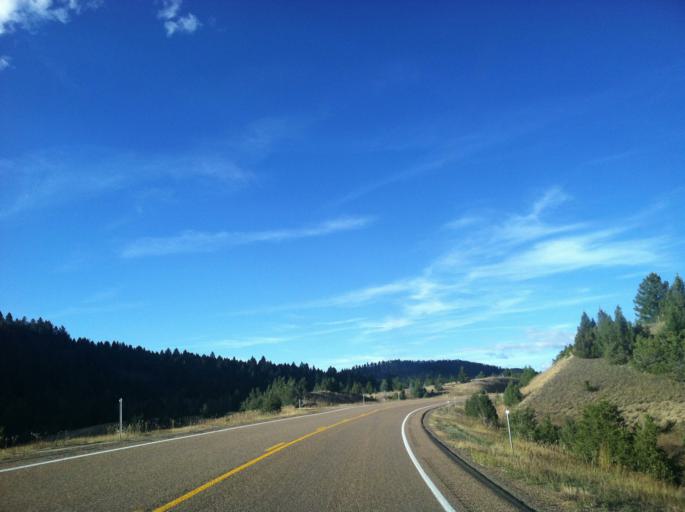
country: US
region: Montana
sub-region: Granite County
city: Philipsburg
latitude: 46.3961
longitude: -113.3080
